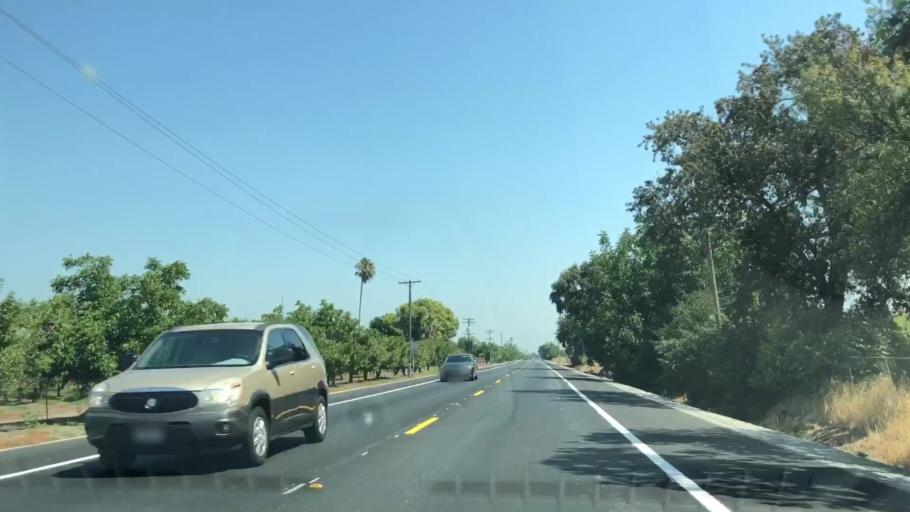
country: US
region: California
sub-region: San Joaquin County
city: Garden Acres
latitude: 37.9474
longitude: -121.2083
